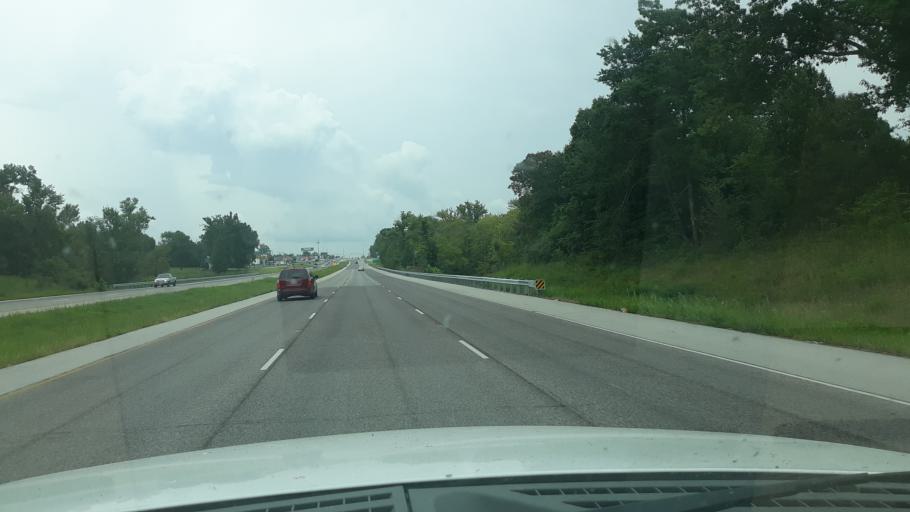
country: US
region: Illinois
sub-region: Williamson County
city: Carterville
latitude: 37.7450
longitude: -89.0888
